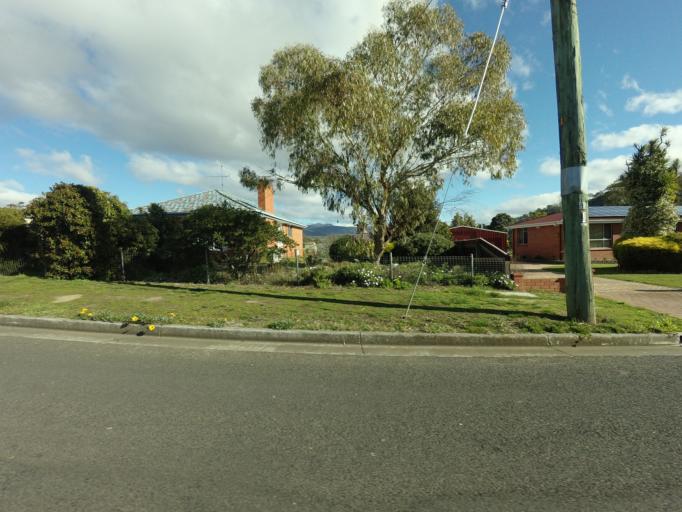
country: AU
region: Tasmania
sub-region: Derwent Valley
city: New Norfolk
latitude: -42.7557
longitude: 147.0512
